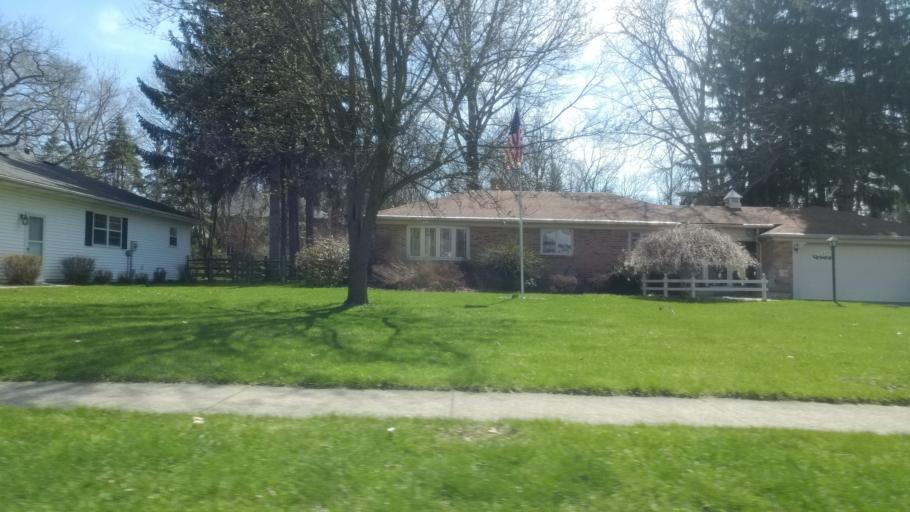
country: US
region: Ohio
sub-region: Wood County
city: Bowling Green
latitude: 41.3788
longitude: -83.6604
